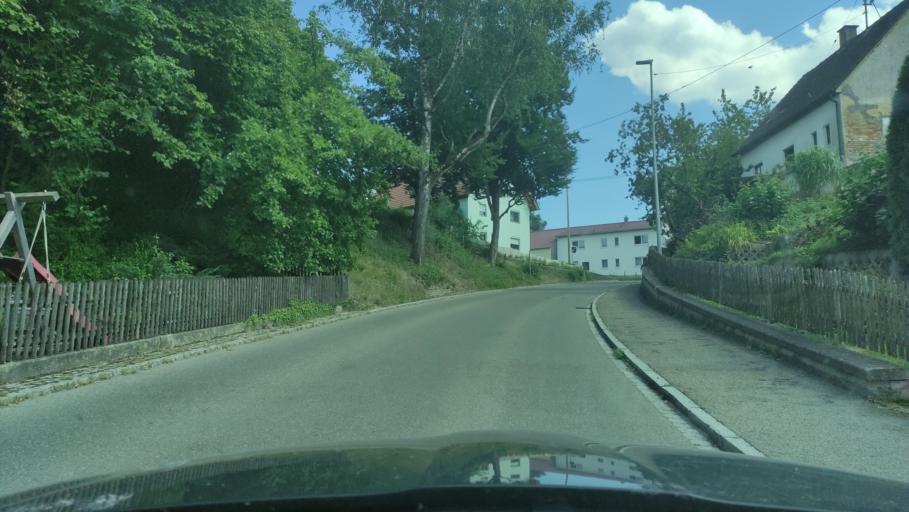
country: DE
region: Bavaria
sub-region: Swabia
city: Deisenhausen
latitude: 48.2895
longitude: 10.3057
